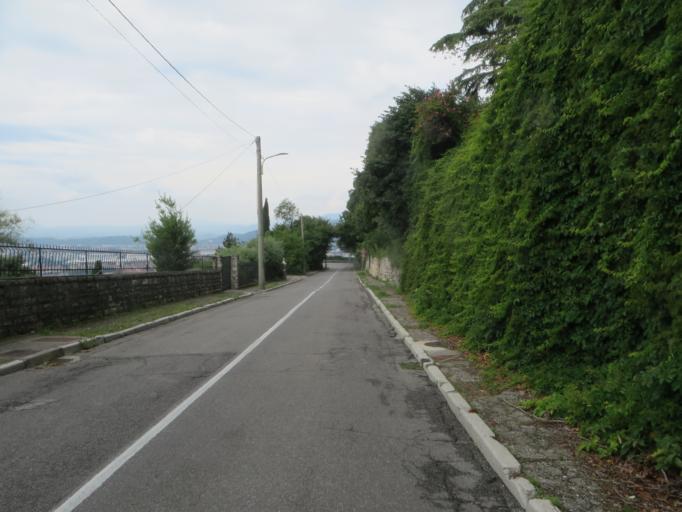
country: IT
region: Lombardy
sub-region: Provincia di Brescia
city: Brescia
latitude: 45.5423
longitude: 10.2391
